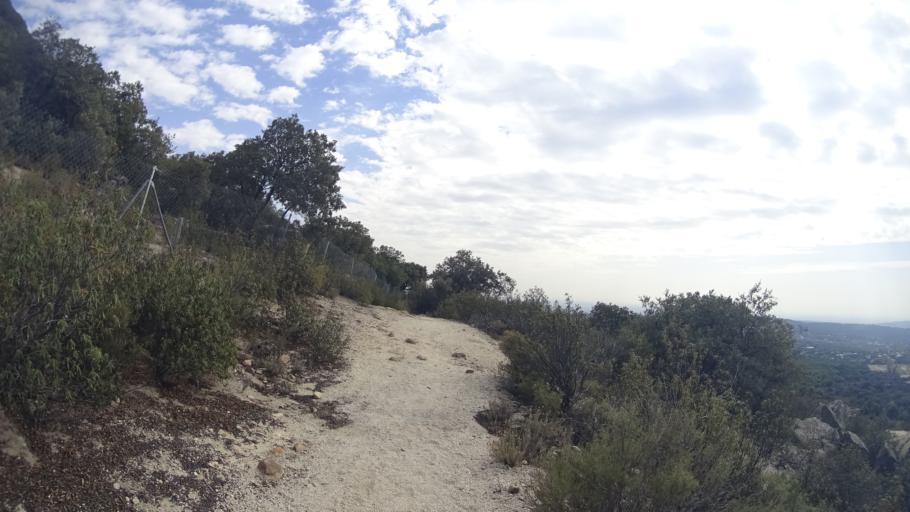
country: ES
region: Madrid
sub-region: Provincia de Madrid
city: Hoyo de Manzanares
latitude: 40.6228
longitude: -3.9294
